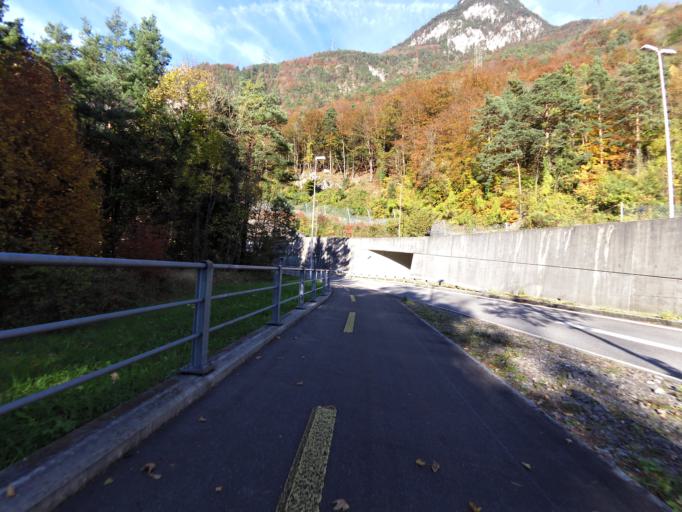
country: CH
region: Uri
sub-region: Uri
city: Flueelen
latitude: 46.9159
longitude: 8.6251
